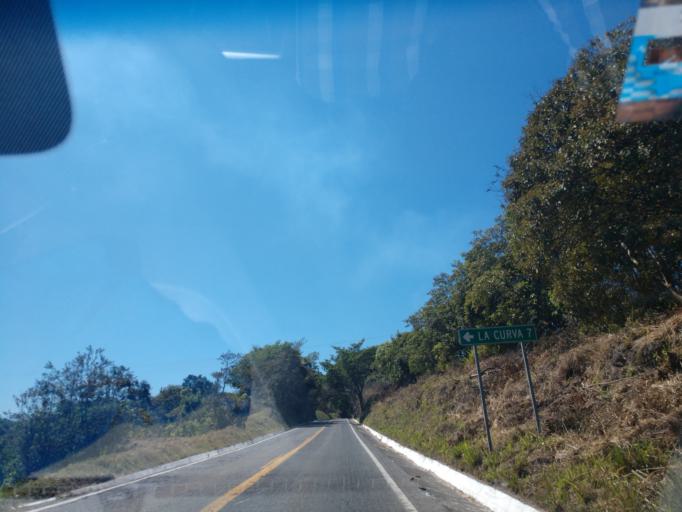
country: MX
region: Nayarit
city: Xalisco
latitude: 21.3754
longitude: -104.8943
